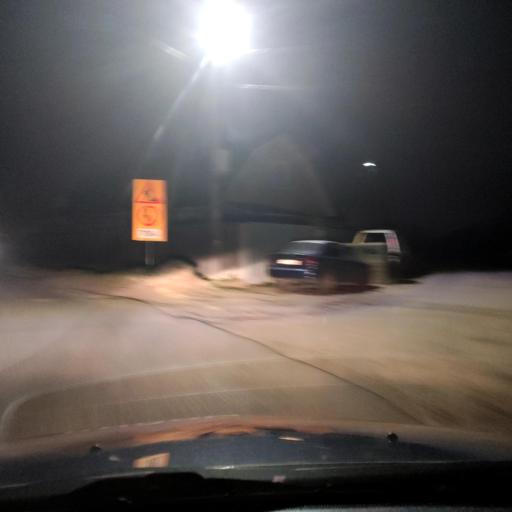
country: RU
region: Voronezj
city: Novaya Usman'
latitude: 51.6401
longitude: 39.3933
